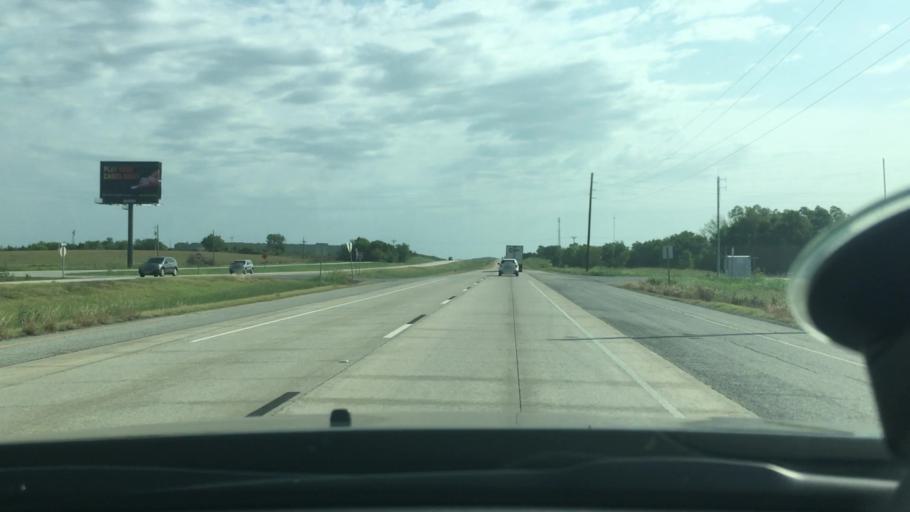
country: US
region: Oklahoma
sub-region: Atoka County
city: Atoka
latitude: 34.4212
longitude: -96.0955
